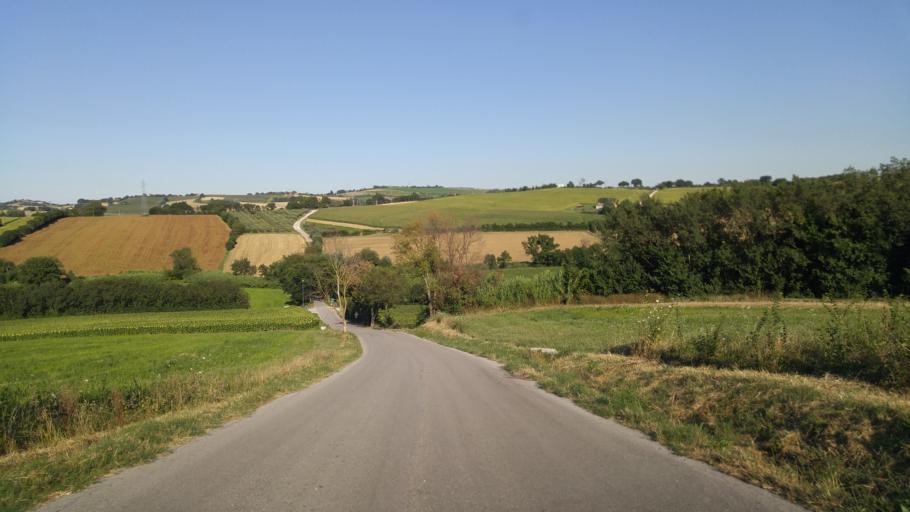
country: IT
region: The Marches
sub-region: Provincia di Pesaro e Urbino
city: Mombaroccio
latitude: 43.8116
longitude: 12.8777
